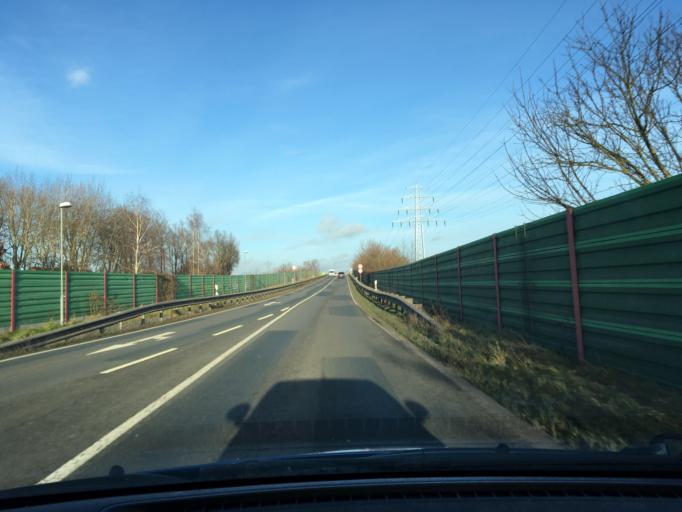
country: DE
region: Lower Saxony
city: Winsen
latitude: 53.3450
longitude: 10.2203
